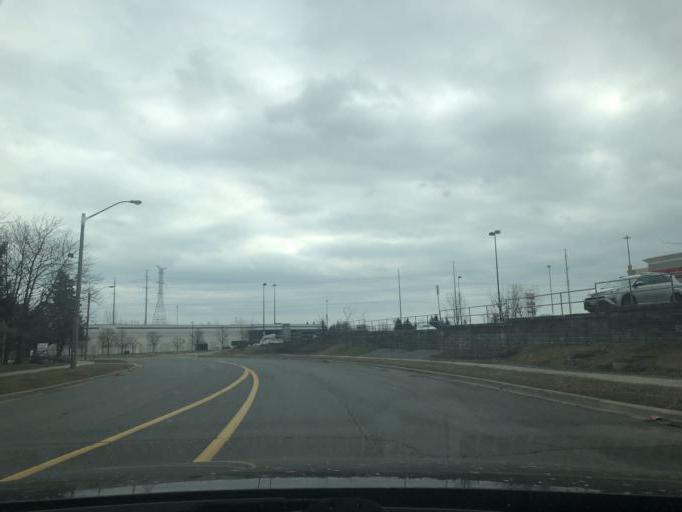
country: CA
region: Ontario
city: Scarborough
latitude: 43.7993
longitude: -79.1963
